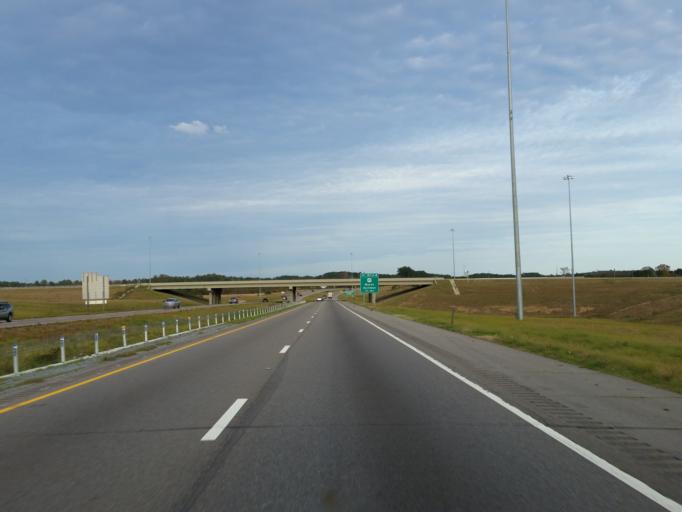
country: US
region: Mississippi
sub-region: Lauderdale County
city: Marion
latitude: 32.3773
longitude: -88.6572
